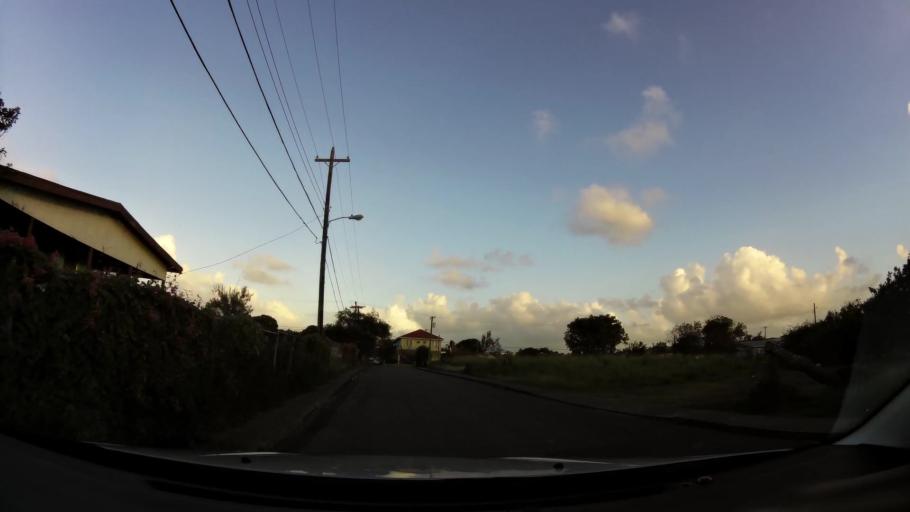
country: AG
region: Saint John
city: Saint John's
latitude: 17.1288
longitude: -61.8454
